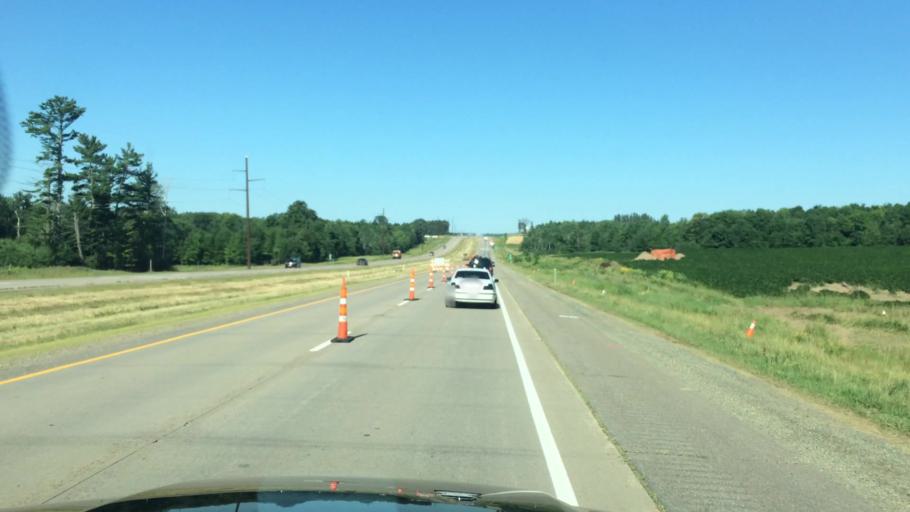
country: US
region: Wisconsin
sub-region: Marathon County
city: Edgar
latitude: 44.9446
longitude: -89.9146
